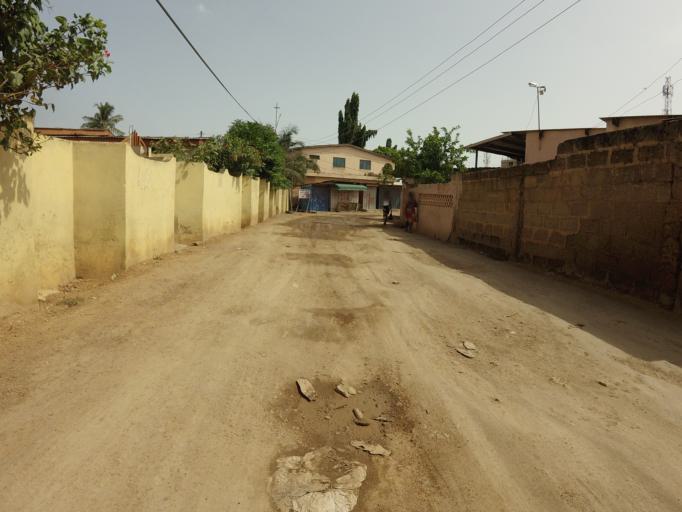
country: GH
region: Greater Accra
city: Dome
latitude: 5.6147
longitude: -0.2398
